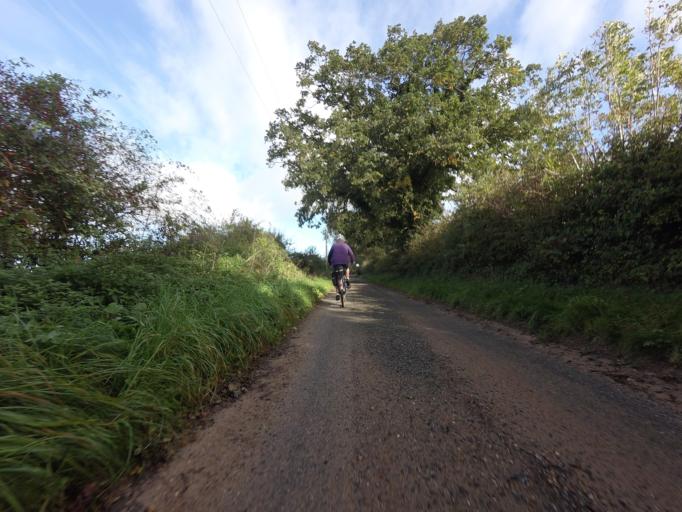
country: GB
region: England
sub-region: Norfolk
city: Dersingham
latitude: 52.8629
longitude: 0.6662
